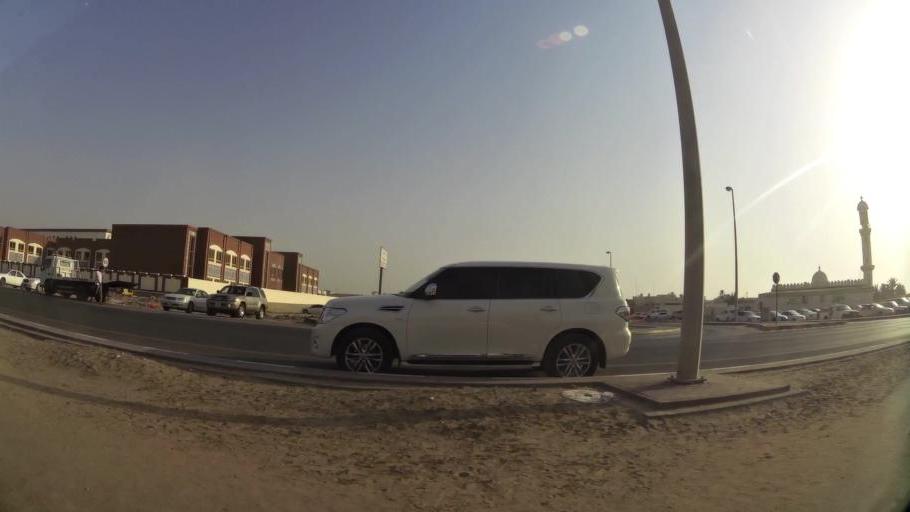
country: AE
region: Ajman
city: Ajman
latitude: 25.3816
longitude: 55.4479
